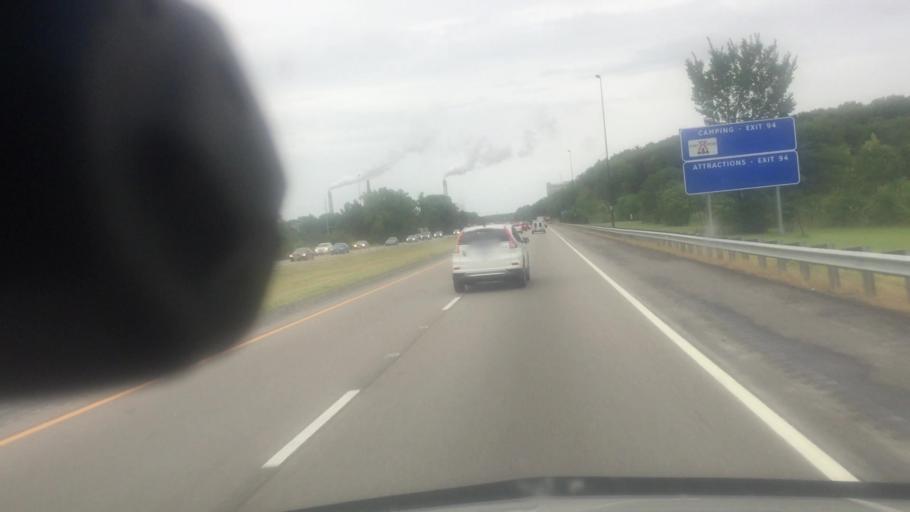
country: US
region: Illinois
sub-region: Sangamon County
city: Grandview
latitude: 39.7781
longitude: -89.6017
